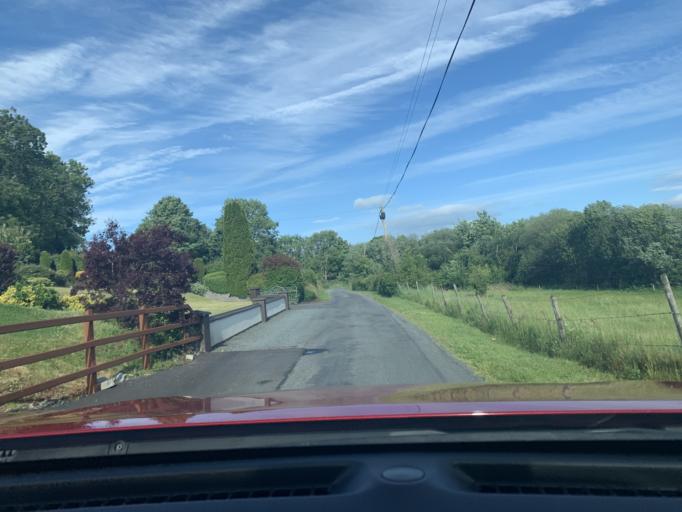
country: IE
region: Connaught
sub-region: Sligo
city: Sligo
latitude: 54.2523
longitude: -8.4999
